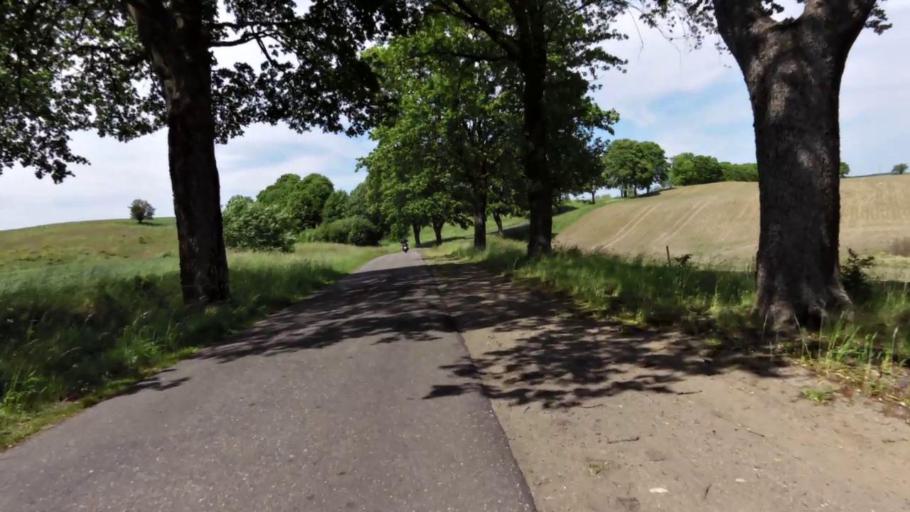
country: PL
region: West Pomeranian Voivodeship
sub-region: Powiat szczecinecki
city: Szczecinek
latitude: 53.6508
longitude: 16.6739
